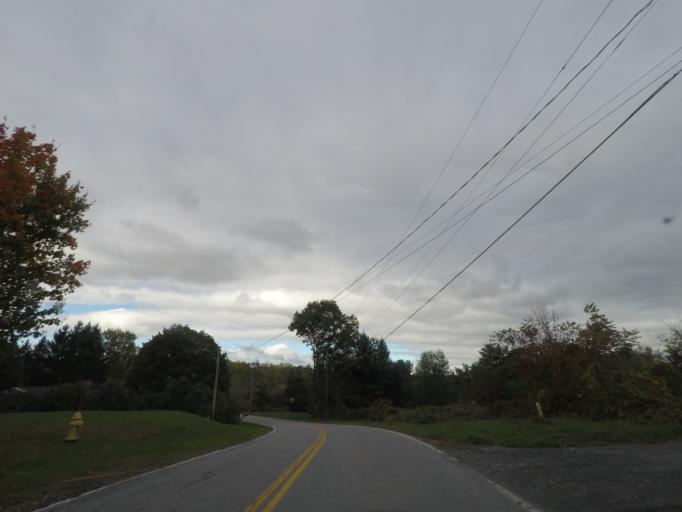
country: US
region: New York
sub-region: Saratoga County
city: Mechanicville
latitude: 42.8800
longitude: -73.7236
